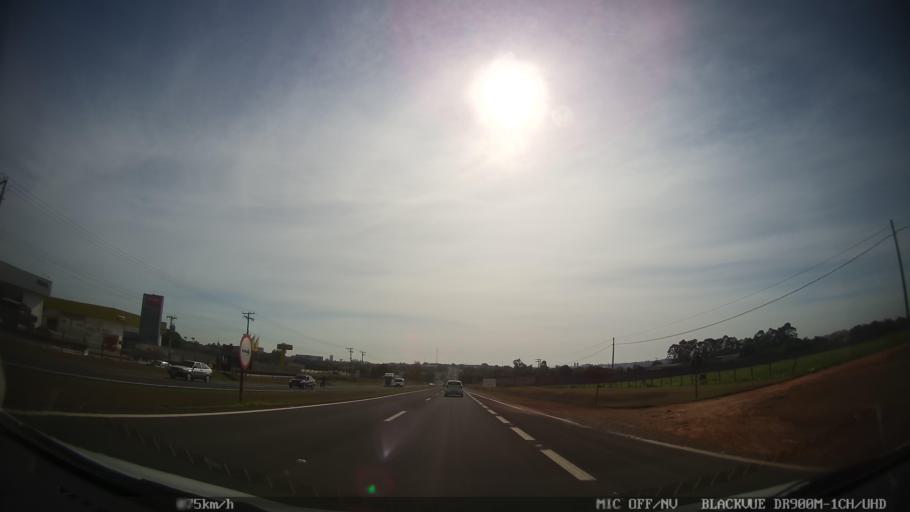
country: BR
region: Sao Paulo
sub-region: Piracicaba
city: Piracicaba
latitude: -22.7776
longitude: -47.6508
